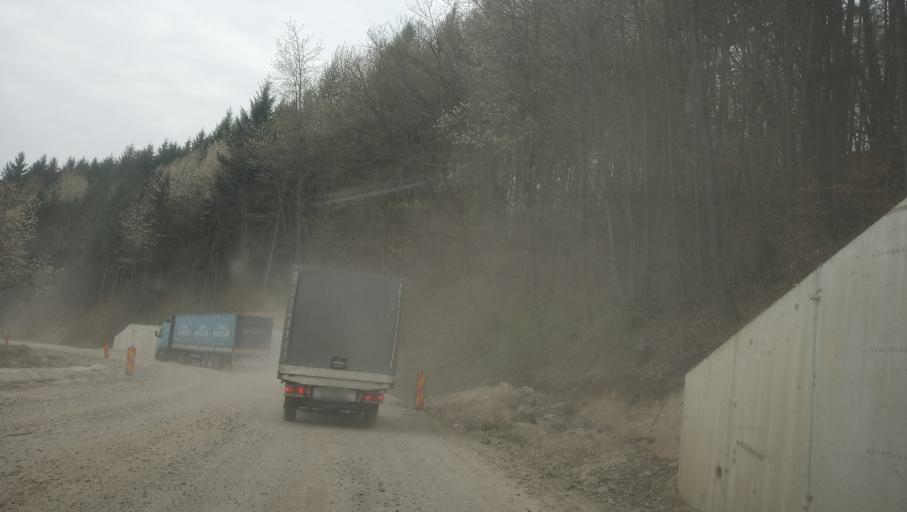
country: RO
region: Bihor
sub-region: Comuna Cristioru de Jos
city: Cristioru de Jos
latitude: 46.3726
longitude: 22.5534
